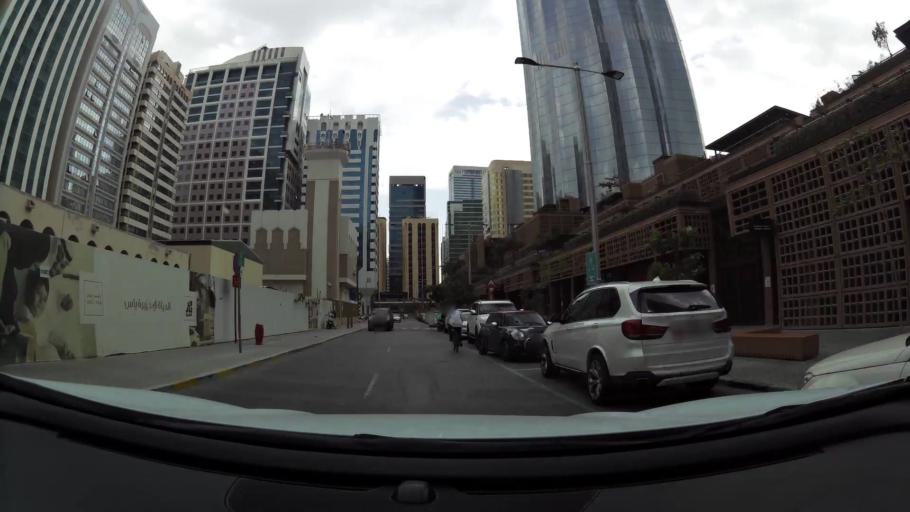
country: AE
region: Abu Dhabi
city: Abu Dhabi
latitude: 24.4881
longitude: 54.3579
